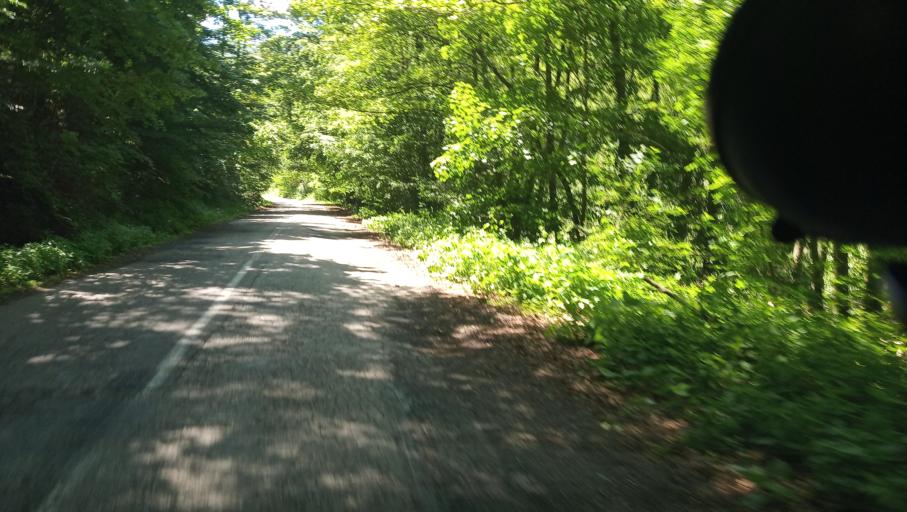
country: RO
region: Mehedinti
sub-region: Comuna Podeni
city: Podeni
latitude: 44.9853
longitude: 22.5060
